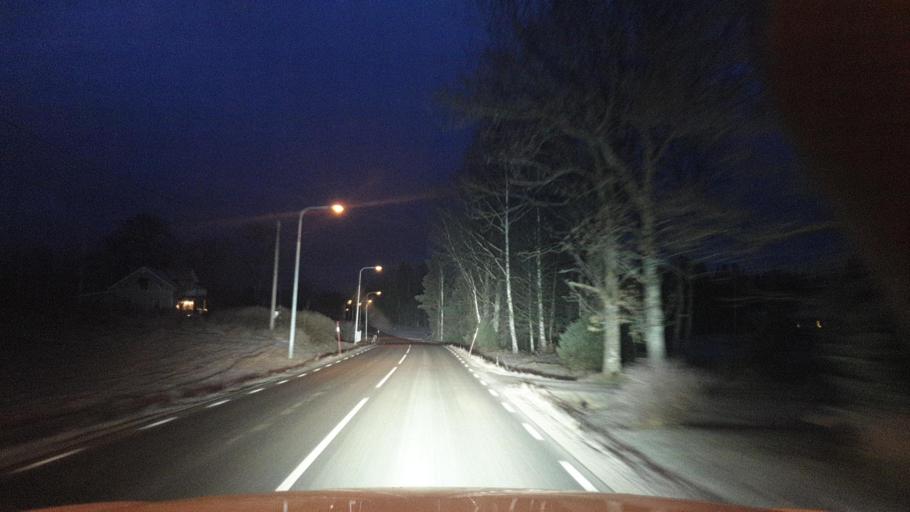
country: SE
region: Vaermland
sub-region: Arvika Kommun
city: Arvika
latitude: 59.5413
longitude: 12.5823
